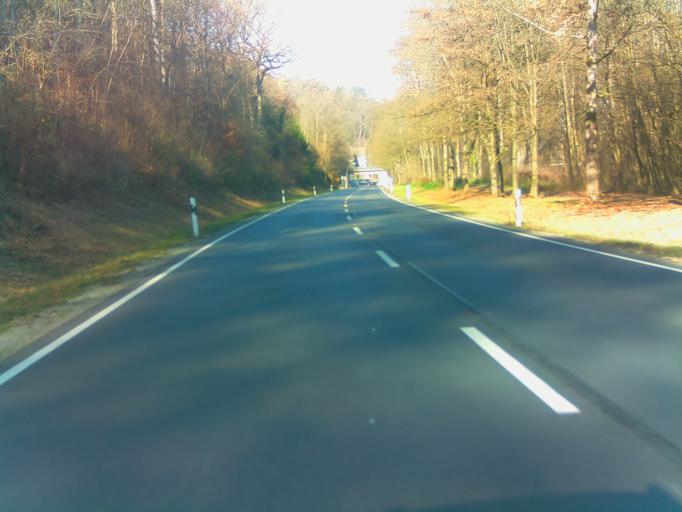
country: DE
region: Bavaria
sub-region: Regierungsbezirk Unterfranken
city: Bad Kissingen
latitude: 50.1840
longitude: 10.0711
